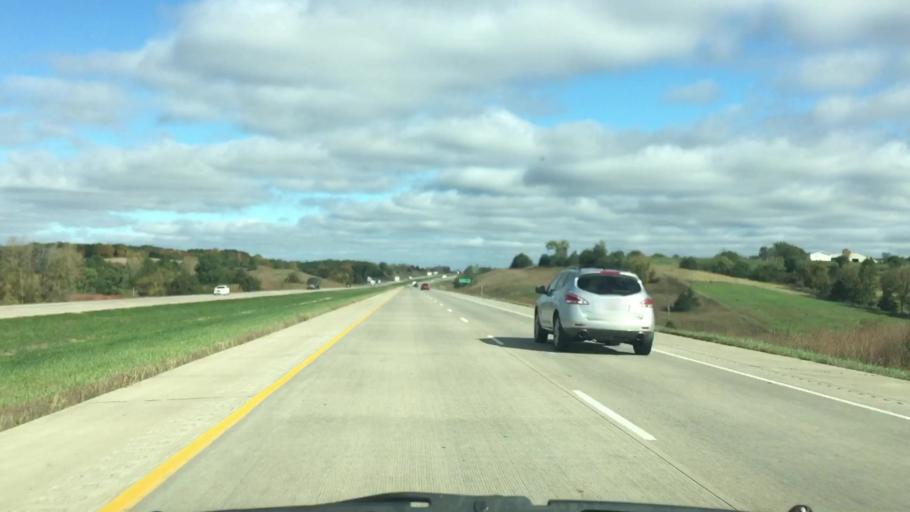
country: US
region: Iowa
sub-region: Decatur County
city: Leon
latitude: 40.8817
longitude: -93.8012
